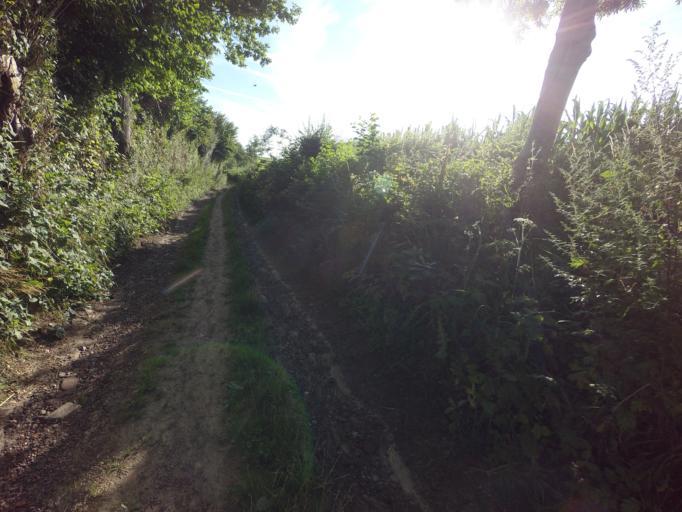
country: NL
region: Limburg
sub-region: Gemeente Vaals
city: Vaals
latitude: 50.7862
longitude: 5.9862
